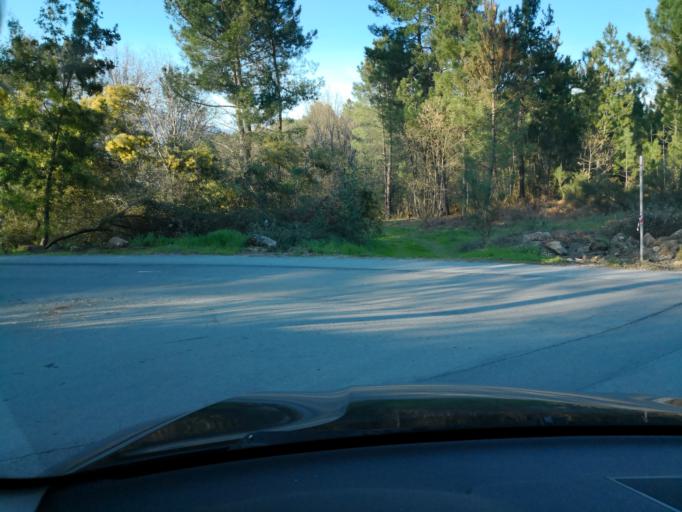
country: PT
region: Vila Real
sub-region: Vila Real
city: Vila Real
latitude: 41.2922
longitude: -7.7769
